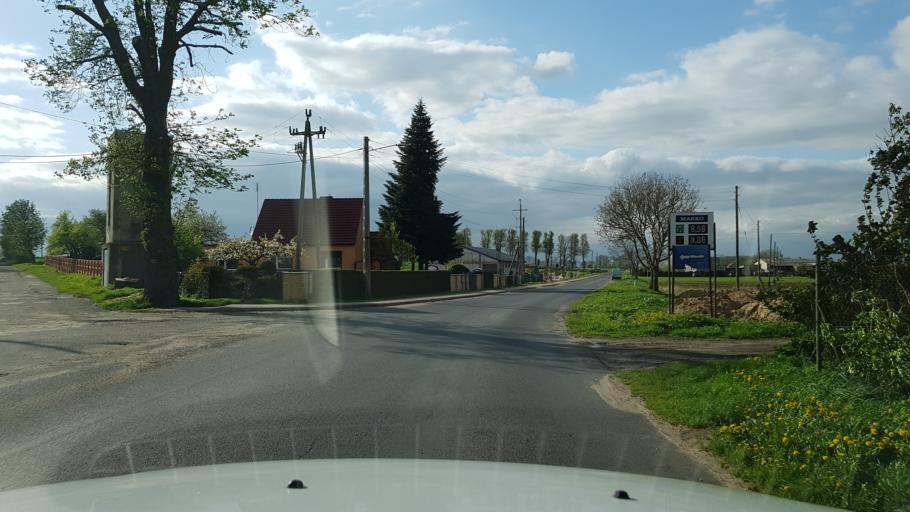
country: PL
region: West Pomeranian Voivodeship
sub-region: Powiat pyrzycki
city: Przelewice
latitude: 53.1063
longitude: 15.0724
